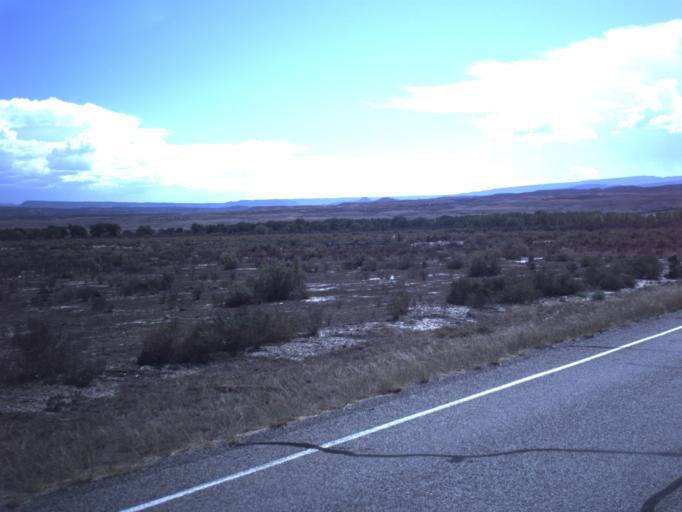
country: US
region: Utah
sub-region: Grand County
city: Moab
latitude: 38.8651
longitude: -109.2948
